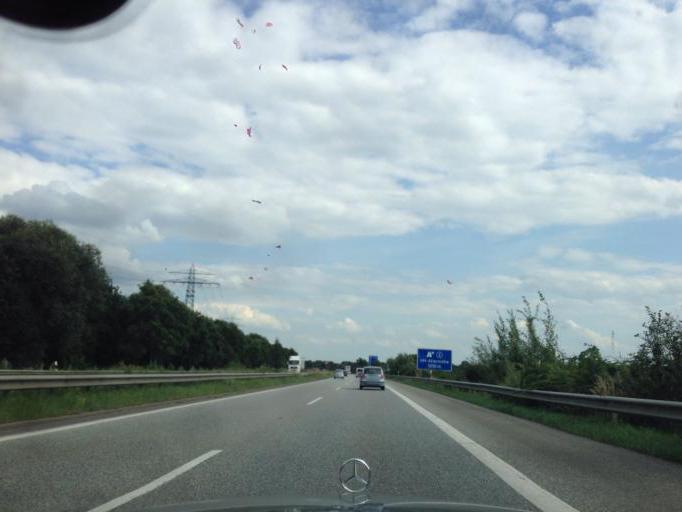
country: DE
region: Hamburg
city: Rothenburgsort
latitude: 53.4931
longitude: 10.1009
